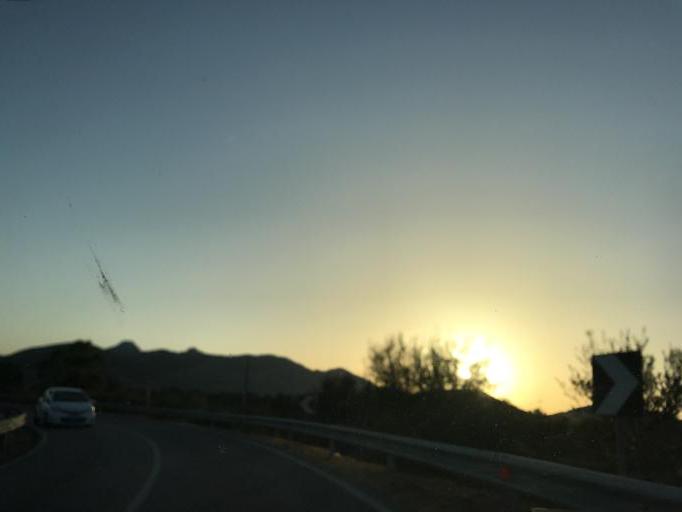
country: IT
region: Sardinia
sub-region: Provincia di Olbia-Tempio
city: San Teodoro
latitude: 40.7654
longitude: 9.6661
